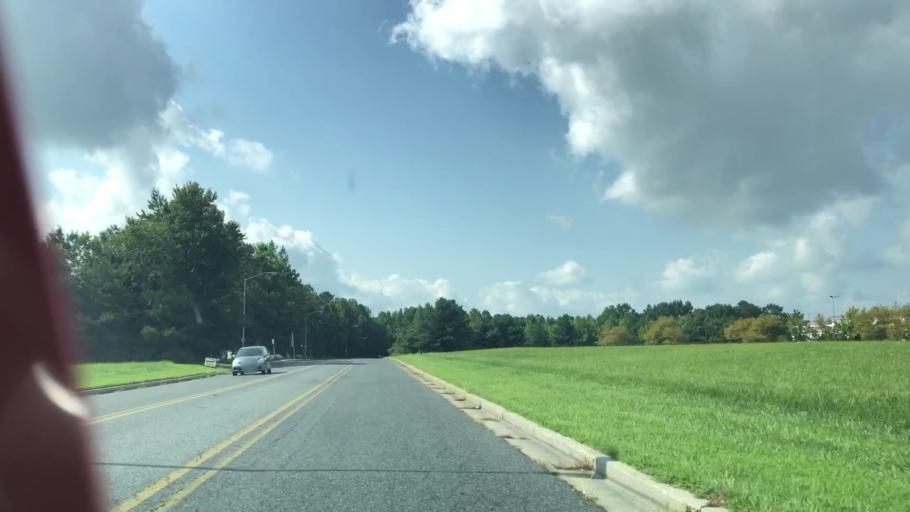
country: US
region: Maryland
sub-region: Wicomico County
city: Salisbury
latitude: 38.3987
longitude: -75.5628
